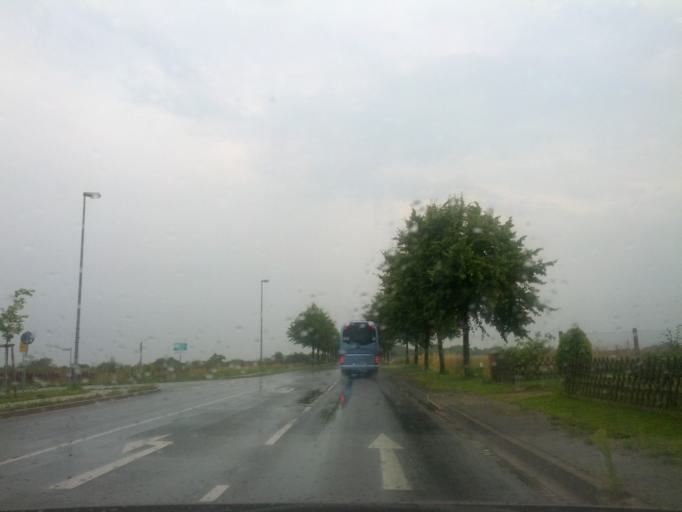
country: DE
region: Mecklenburg-Vorpommern
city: Ostseebad Kuhlungsborn
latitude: 54.1399
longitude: 11.7405
